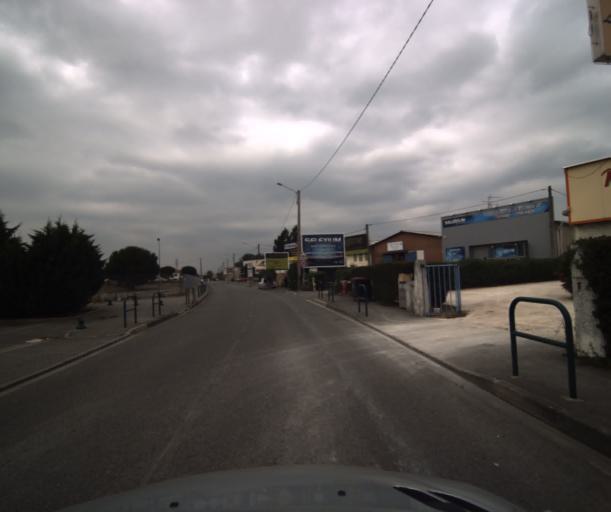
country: FR
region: Midi-Pyrenees
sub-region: Departement de la Haute-Garonne
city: Portet-sur-Garonne
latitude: 43.5367
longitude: 1.4038
